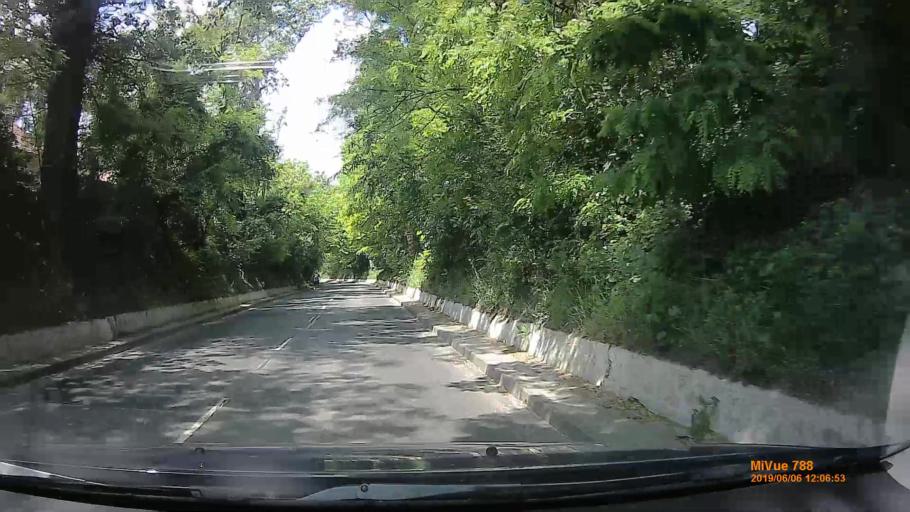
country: HU
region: Pest
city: Kerepes
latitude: 47.5642
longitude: 19.2758
